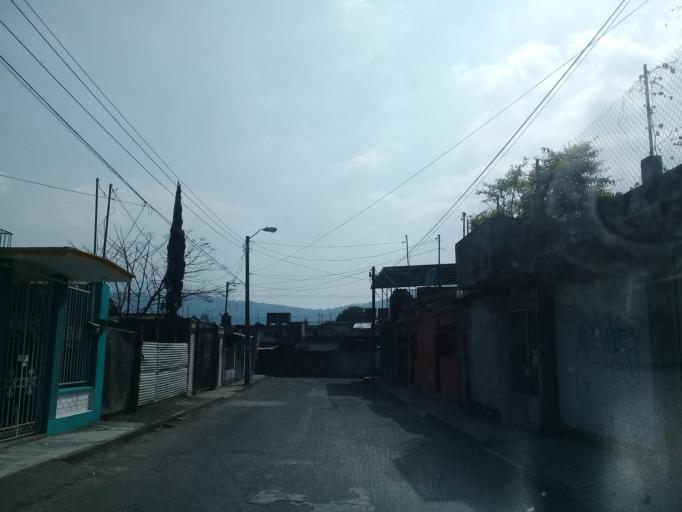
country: MX
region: Veracruz
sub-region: Mariano Escobedo
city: Palmira
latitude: 18.8708
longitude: -97.1046
